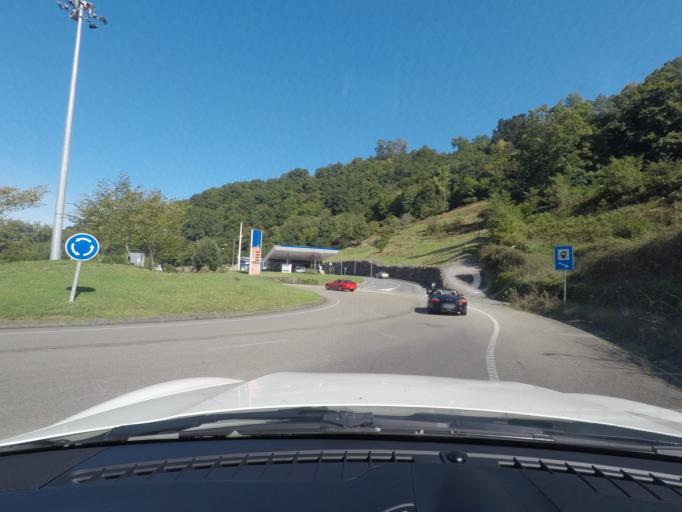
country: ES
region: Asturias
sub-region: Province of Asturias
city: Cangas de Onis
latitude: 43.3531
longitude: -5.1249
